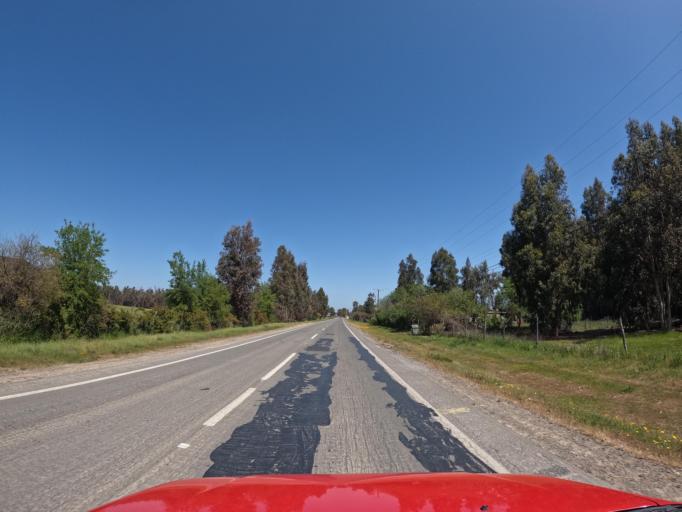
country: CL
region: O'Higgins
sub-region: Provincia de Colchagua
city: Santa Cruz
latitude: -34.7320
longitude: -71.6818
